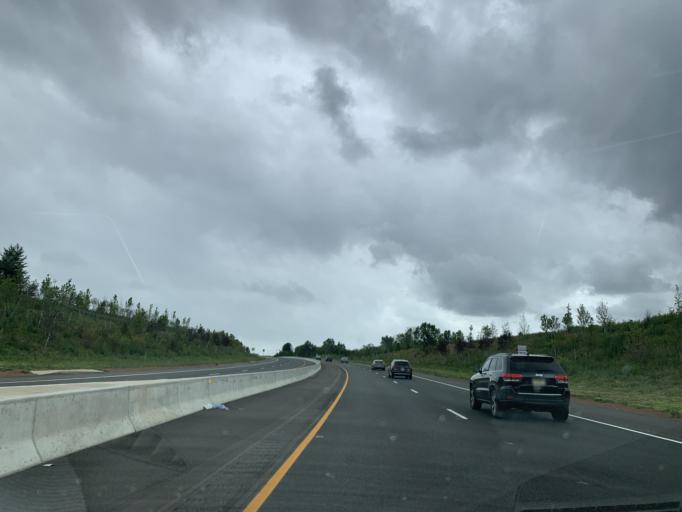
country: US
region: New Jersey
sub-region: Somerset County
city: Bloomingdale
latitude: 40.5066
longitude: -74.6348
